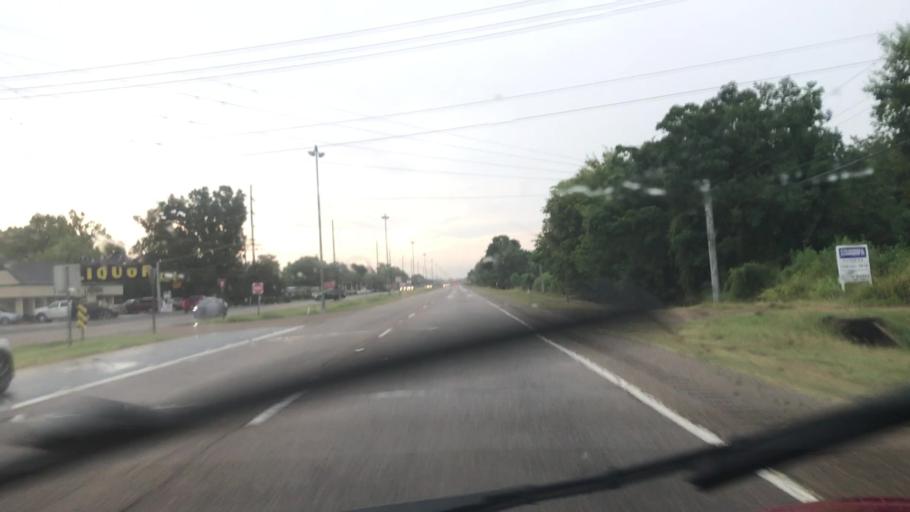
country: US
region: Louisiana
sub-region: Bossier Parish
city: Red Chute
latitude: 32.5375
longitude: -93.6596
